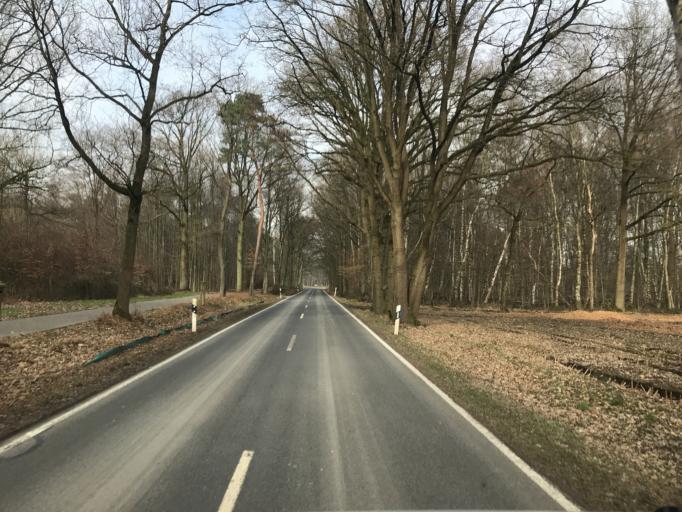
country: DE
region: North Rhine-Westphalia
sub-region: Regierungsbezirk Dusseldorf
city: Grefrath
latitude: 51.3680
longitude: 6.3628
